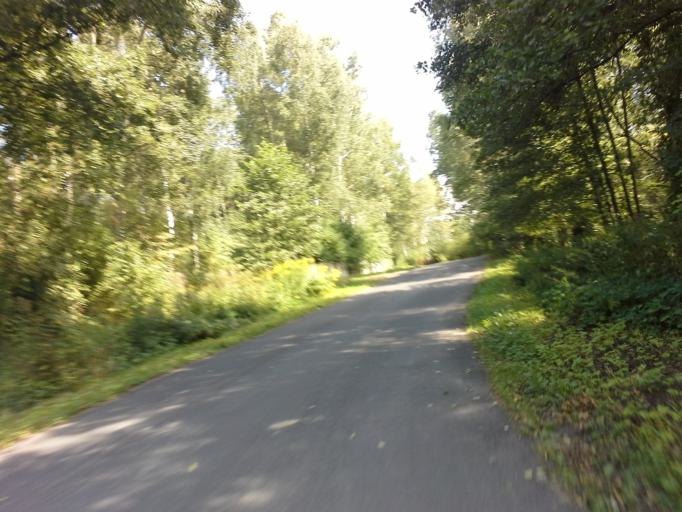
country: PL
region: Lesser Poland Voivodeship
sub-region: Powiat chrzanowski
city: Trzebinia
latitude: 50.1369
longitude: 19.4441
